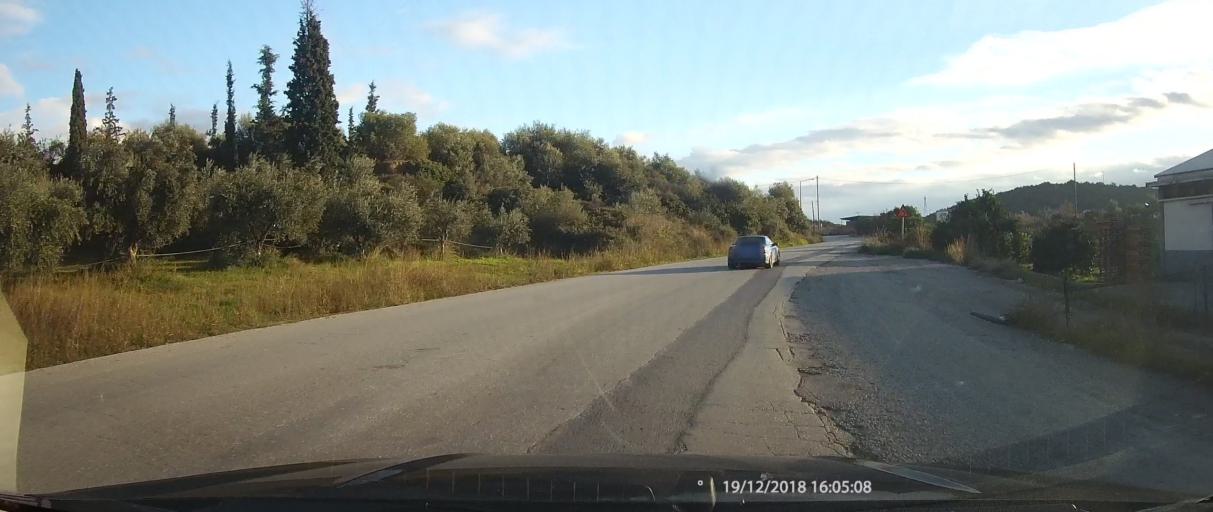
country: GR
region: Peloponnese
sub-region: Nomos Lakonias
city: Vlakhiotis
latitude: 36.8621
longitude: 22.7178
